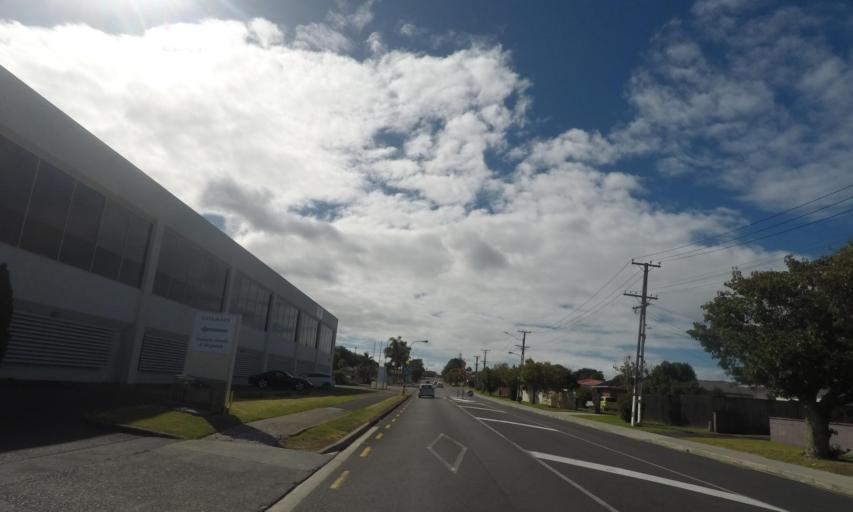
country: NZ
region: Auckland
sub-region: Auckland
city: Tamaki
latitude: -36.9126
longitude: 174.8457
